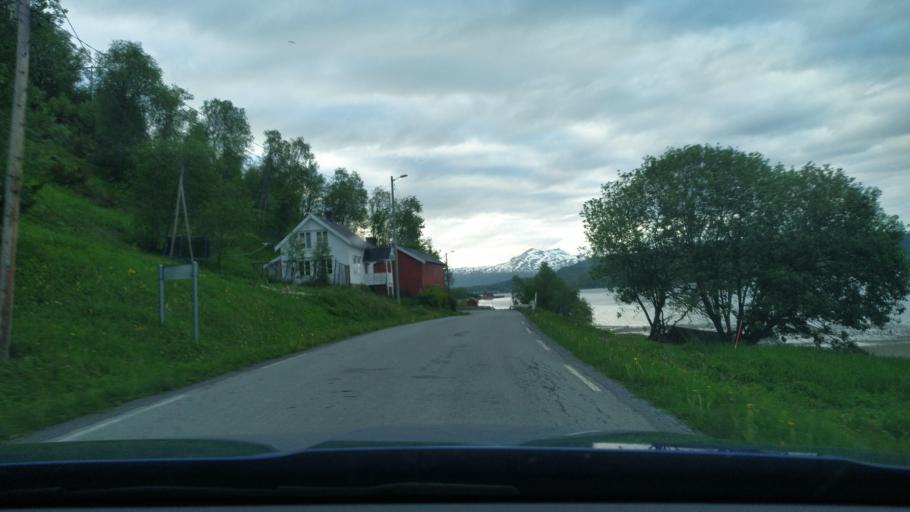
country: NO
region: Troms
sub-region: Sorreisa
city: Sorreisa
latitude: 69.1383
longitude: 18.0578
